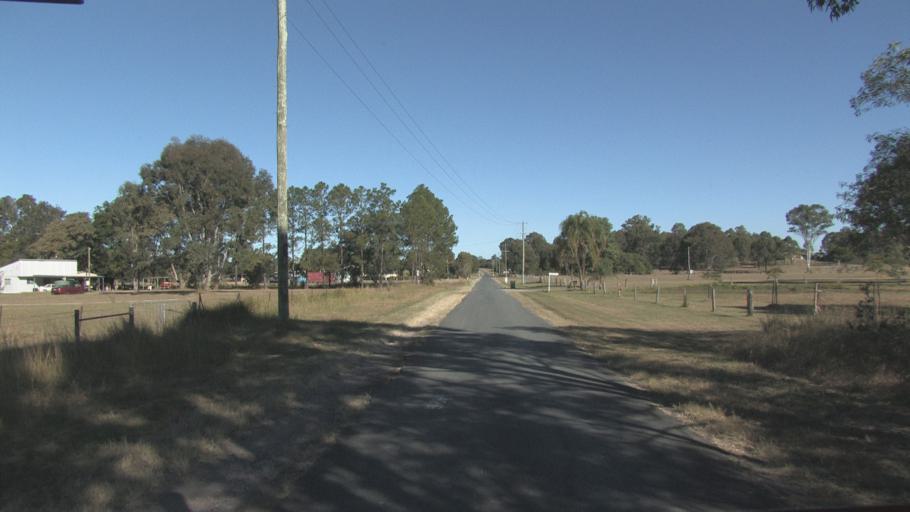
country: AU
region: Queensland
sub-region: Logan
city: North Maclean
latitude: -27.7771
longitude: 153.0197
